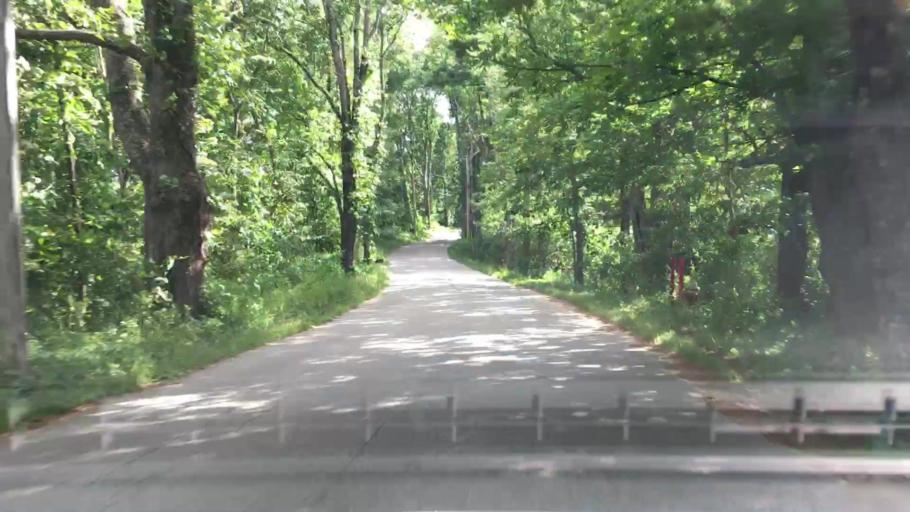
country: US
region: New Hampshire
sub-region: Strafford County
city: Madbury
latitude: 43.1652
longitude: -70.9165
